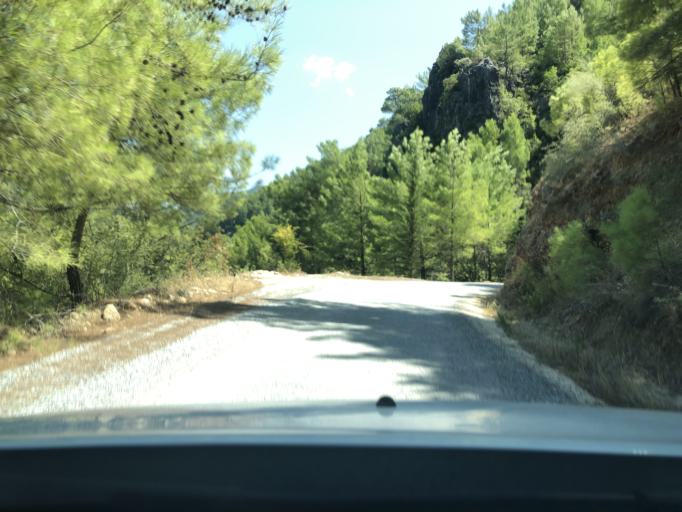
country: TR
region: Antalya
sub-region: Manavgat
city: Manavgat
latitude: 36.9073
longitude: 31.5556
